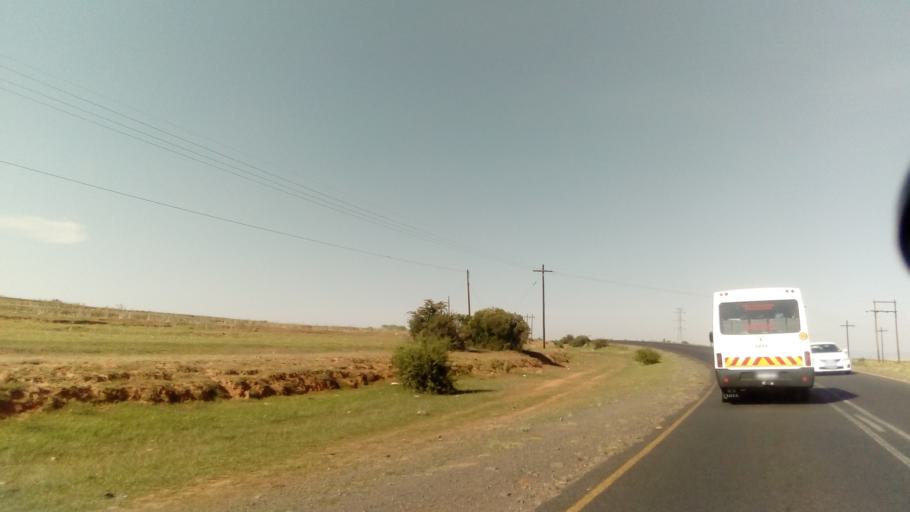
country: LS
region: Berea
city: Teyateyaneng
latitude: -29.1534
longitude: 27.6595
